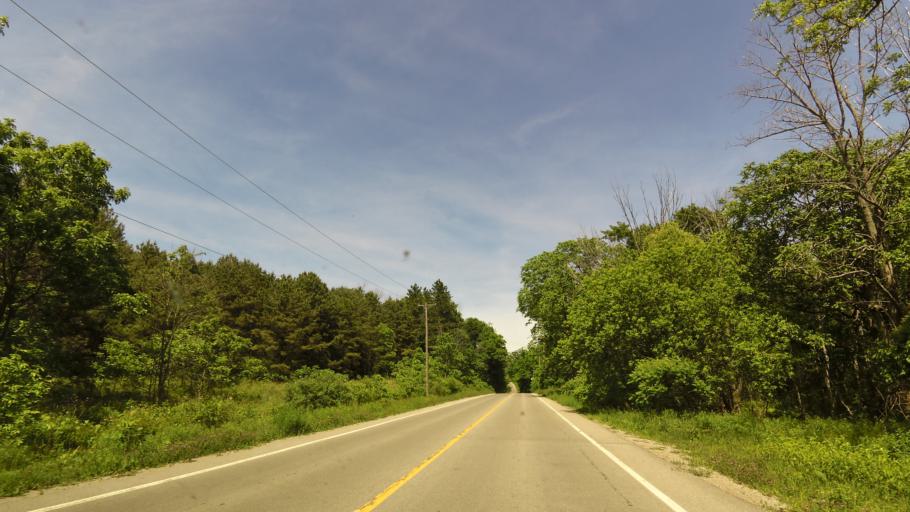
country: CA
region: Ontario
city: Norfolk County
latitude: 42.6950
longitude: -80.3454
